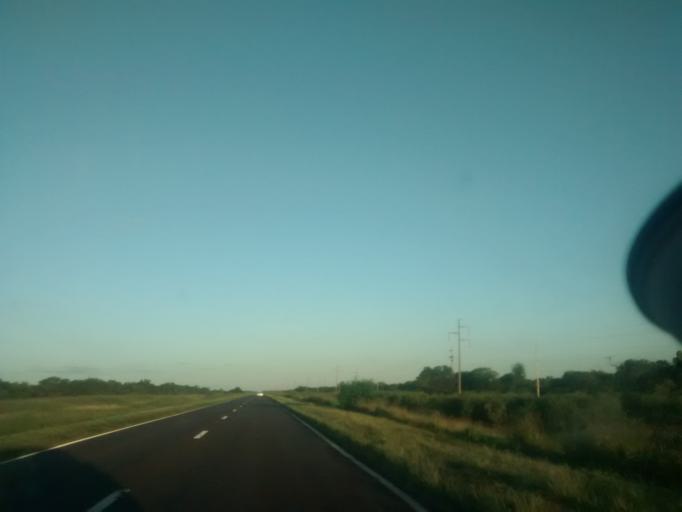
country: AR
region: Chaco
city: La Escondida
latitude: -27.0885
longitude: -59.6396
